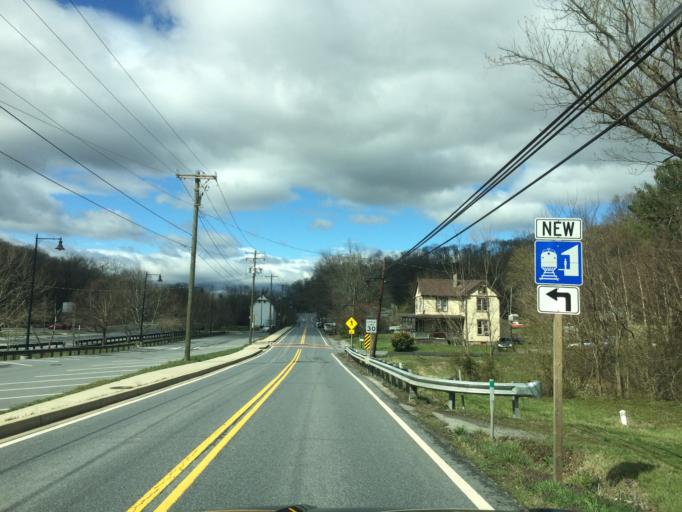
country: US
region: Maryland
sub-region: Frederick County
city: Point of Rocks
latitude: 39.2744
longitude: -77.5360
